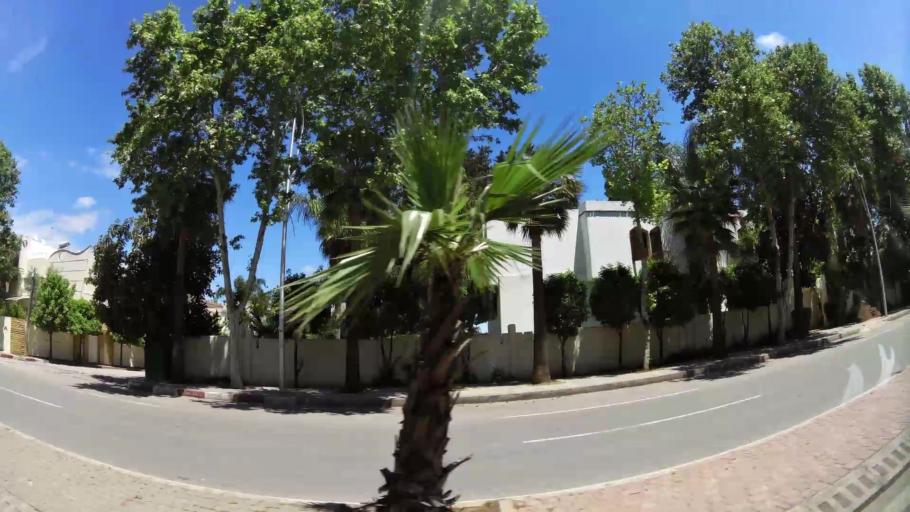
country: MA
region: Fes-Boulemane
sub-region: Fes
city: Fes
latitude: 34.0082
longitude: -4.9950
